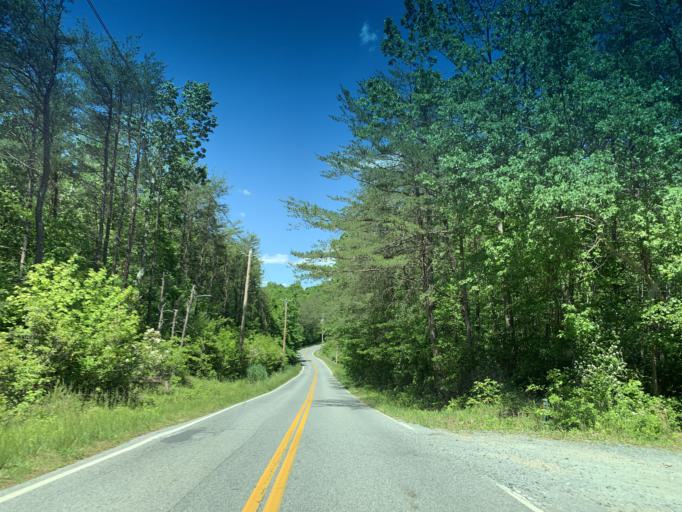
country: US
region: Maryland
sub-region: Cecil County
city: Charlestown
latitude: 39.5332
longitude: -75.9315
